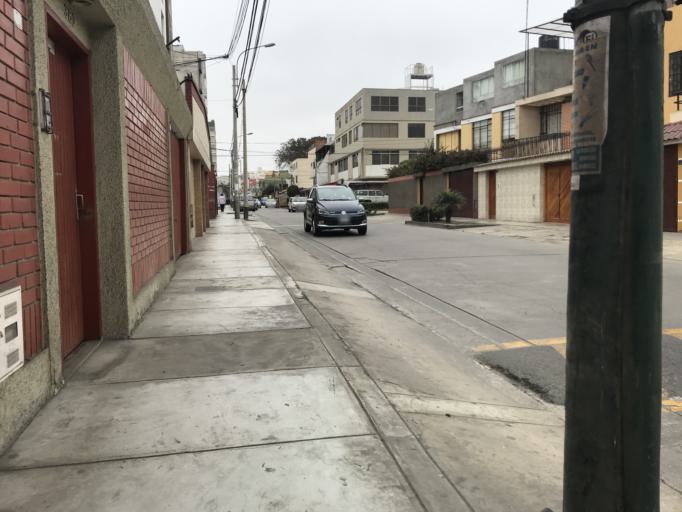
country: PE
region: Lima
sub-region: Lima
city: San Isidro
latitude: -12.0796
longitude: -77.0681
